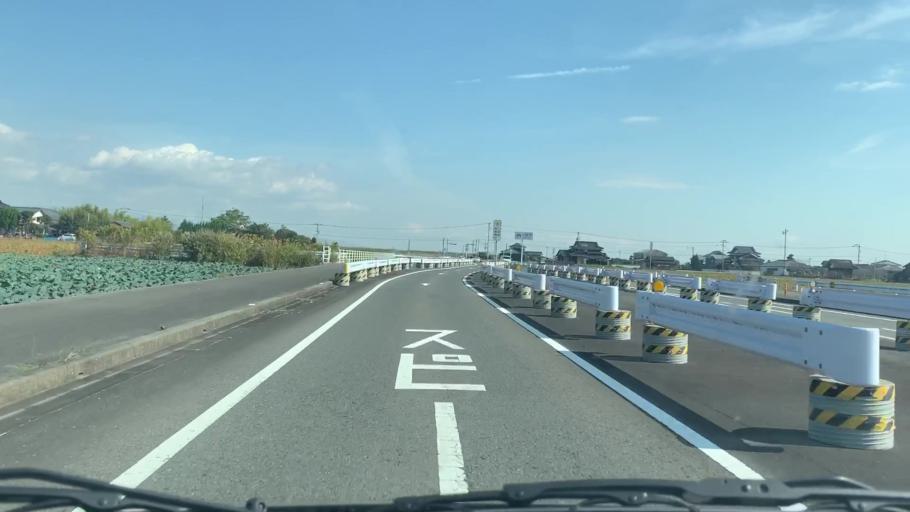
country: JP
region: Saga Prefecture
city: Saga-shi
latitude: 33.2222
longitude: 130.1822
